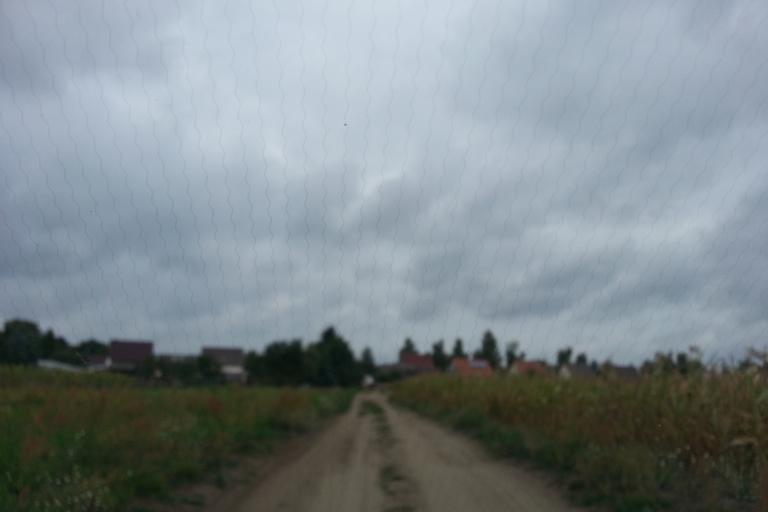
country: DE
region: Mecklenburg-Vorpommern
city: Ferdinandshof
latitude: 53.6564
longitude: 13.8866
